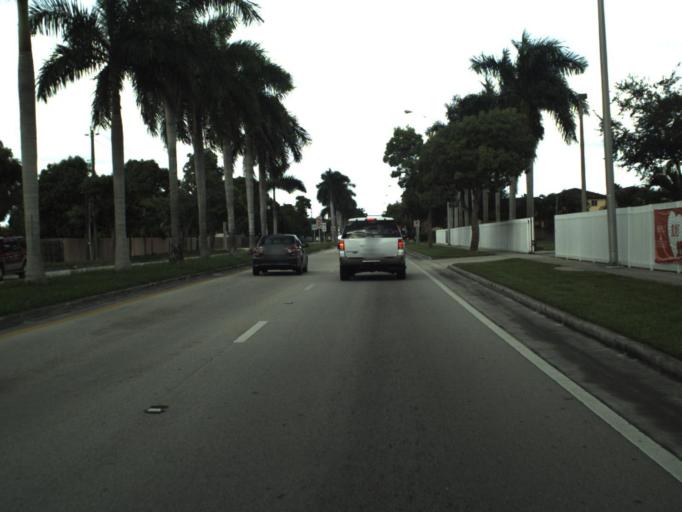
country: US
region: Florida
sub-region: Miami-Dade County
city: Palm Springs North
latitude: 25.9424
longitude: -80.3374
